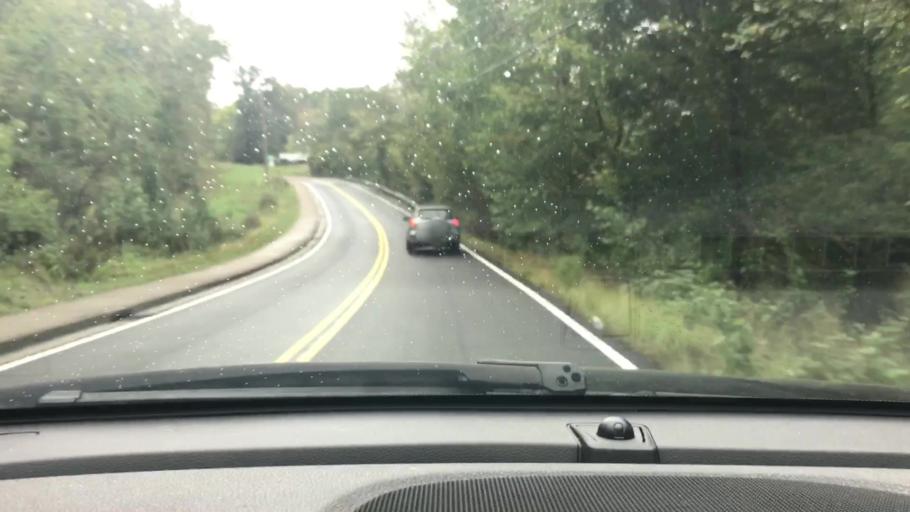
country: US
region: Tennessee
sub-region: Cheatham County
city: Kingston Springs
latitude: 36.0925
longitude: -87.1106
